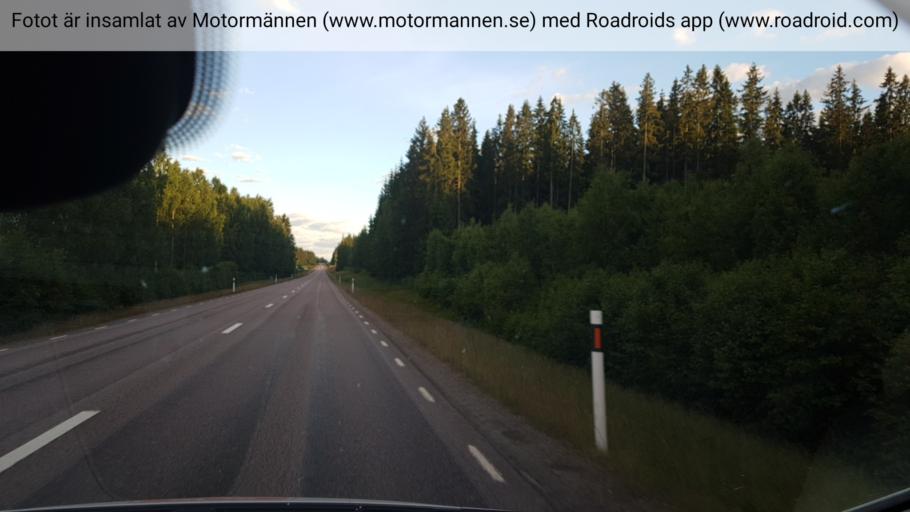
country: SE
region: Vaermland
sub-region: Torsby Kommun
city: Torsby
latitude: 60.0133
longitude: 13.0811
